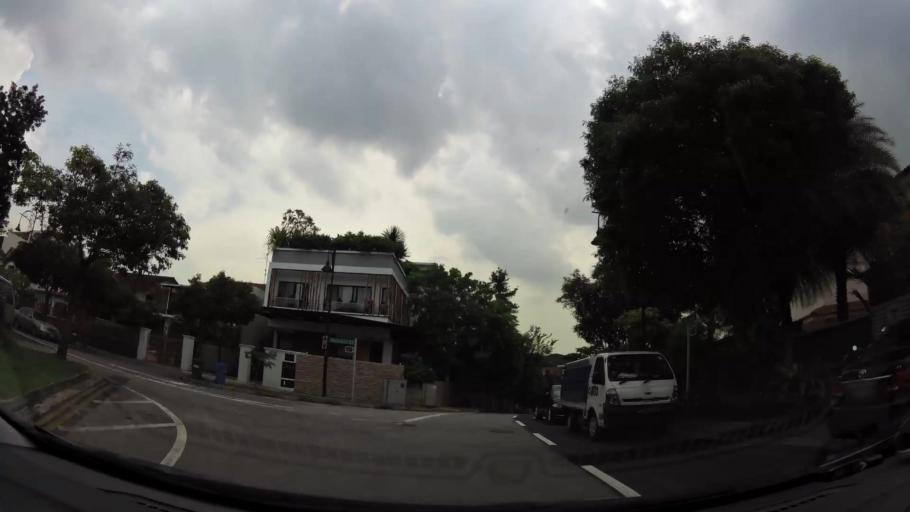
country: SG
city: Singapore
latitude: 1.3464
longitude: 103.8667
